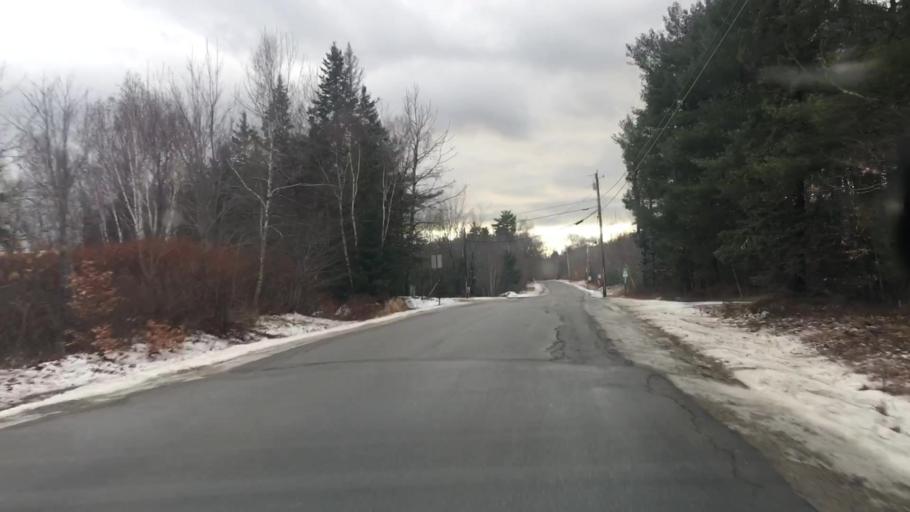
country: US
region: Maine
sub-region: Hancock County
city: Dedham
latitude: 44.6469
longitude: -68.7055
